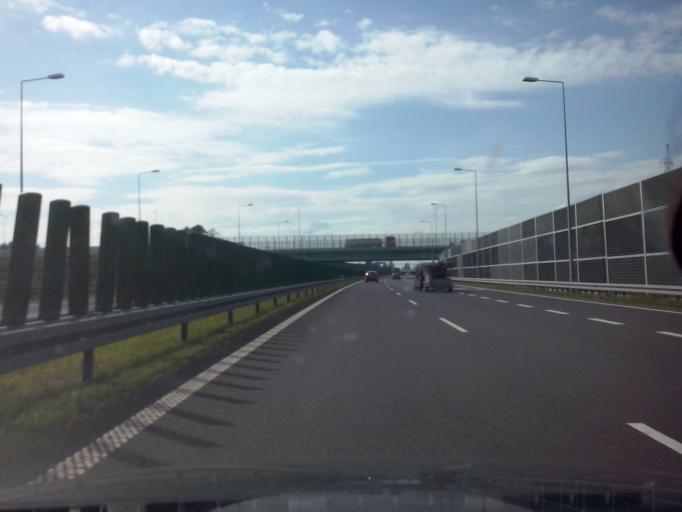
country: PL
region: Lesser Poland Voivodeship
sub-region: Powiat tarnowski
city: Lisia Gora
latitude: 50.0539
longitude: 21.0135
